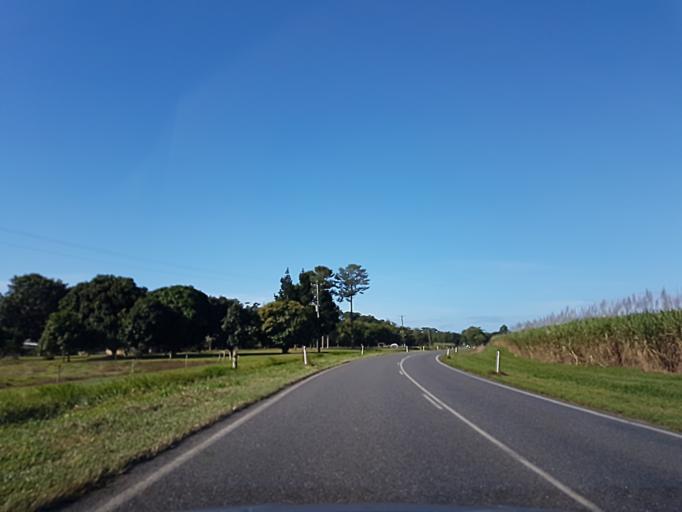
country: AU
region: Queensland
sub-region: Cairns
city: Port Douglas
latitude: -16.4366
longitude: 145.3803
